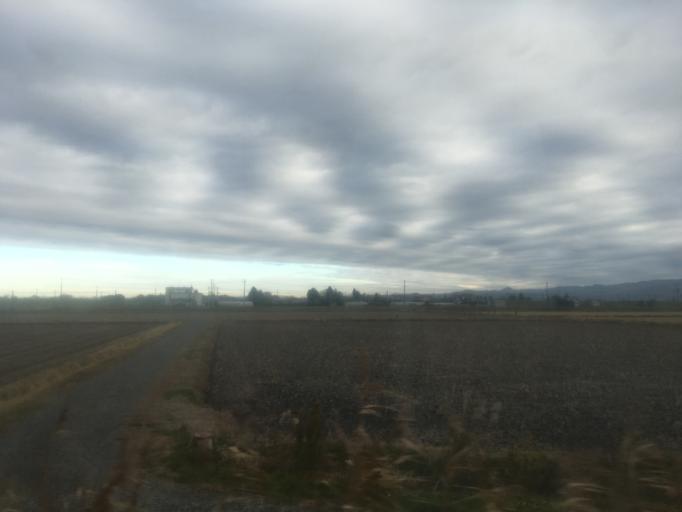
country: JP
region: Miyagi
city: Yamoto
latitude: 38.4966
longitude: 141.2443
